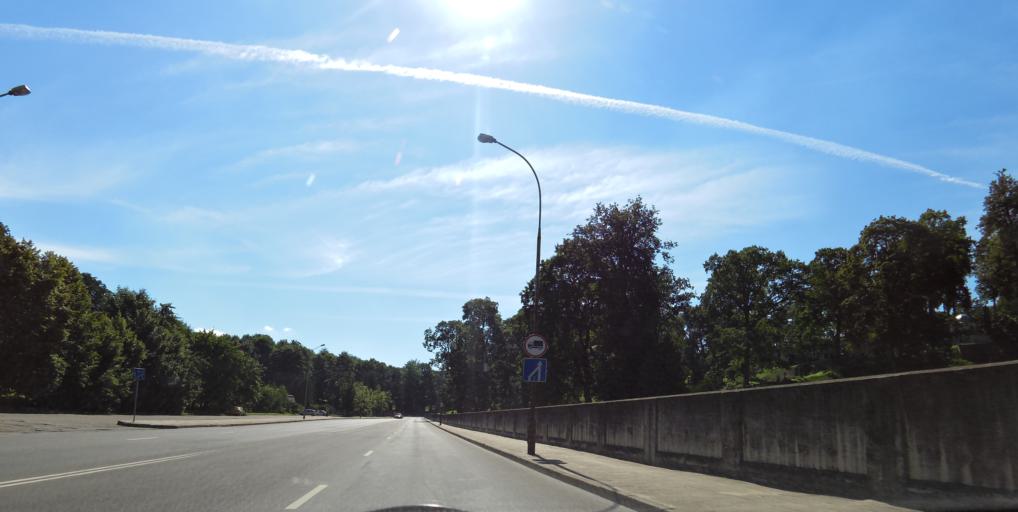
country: LT
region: Vilnius County
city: Rasos
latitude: 54.6707
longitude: 25.3048
